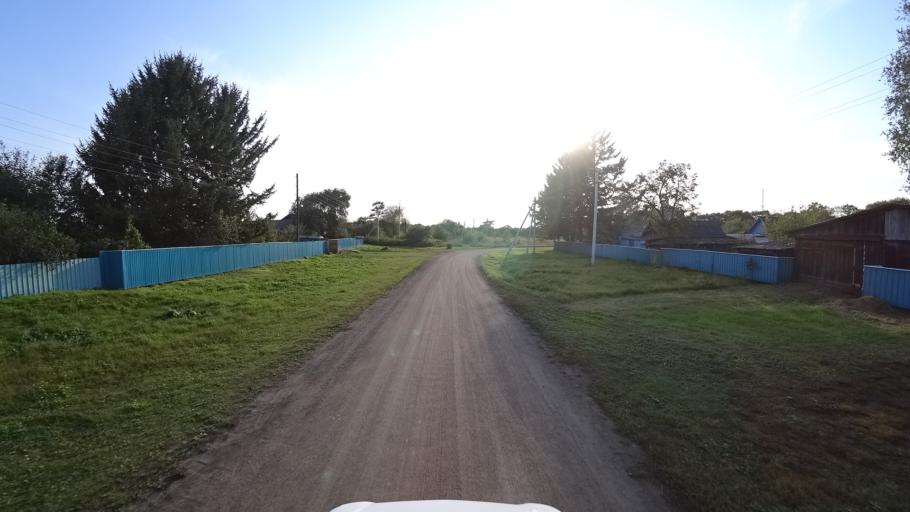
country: RU
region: Amur
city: Arkhara
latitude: 49.3613
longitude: 130.1264
